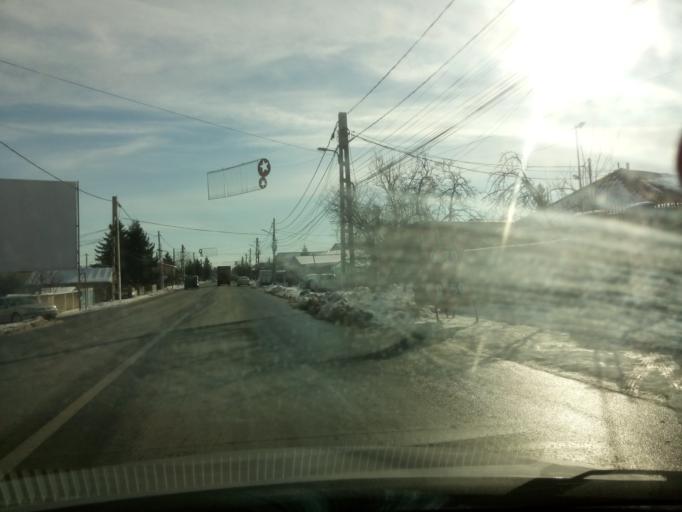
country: RO
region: Ilfov
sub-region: Comuna Popesti-Leordeni
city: Popesti-Leordeni
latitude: 44.3767
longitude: 26.1740
